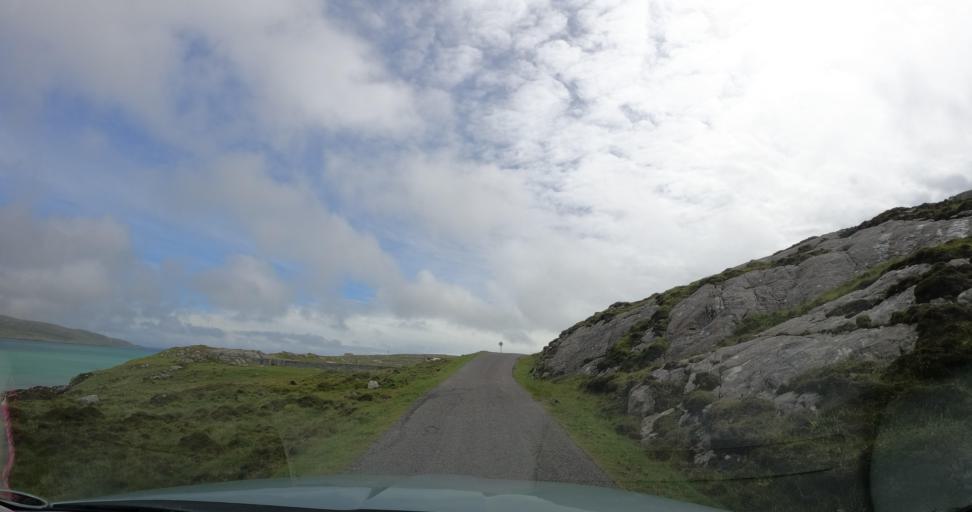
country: GB
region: Scotland
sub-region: Eilean Siar
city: Barra
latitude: 56.9362
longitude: -7.5202
